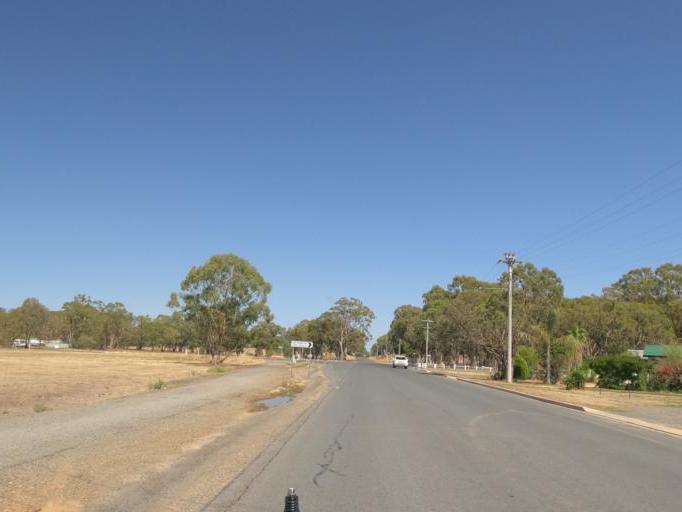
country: AU
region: New South Wales
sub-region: Corowa Shire
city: Mulwala
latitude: -35.9916
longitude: 145.9970
